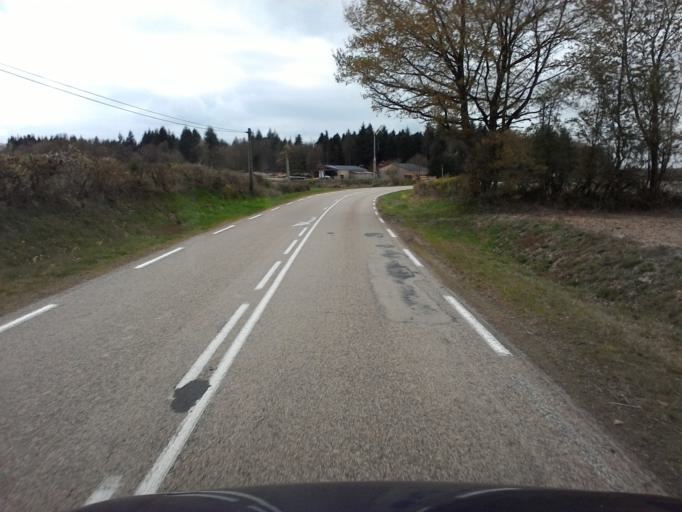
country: FR
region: Bourgogne
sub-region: Departement de l'Yonne
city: Avallon
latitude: 47.3329
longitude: 4.0258
